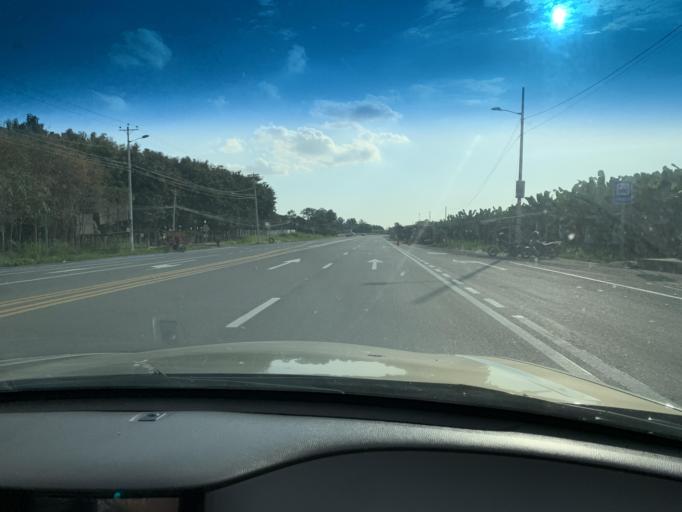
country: EC
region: Guayas
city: Naranjito
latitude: -2.2572
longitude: -79.5618
